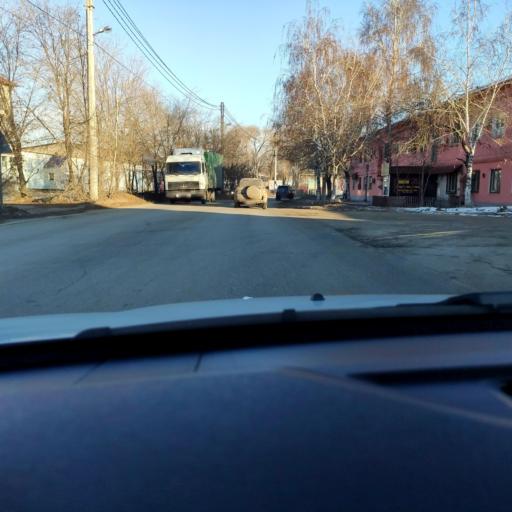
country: RU
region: Samara
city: Petra-Dubrava
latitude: 53.2431
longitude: 50.2982
